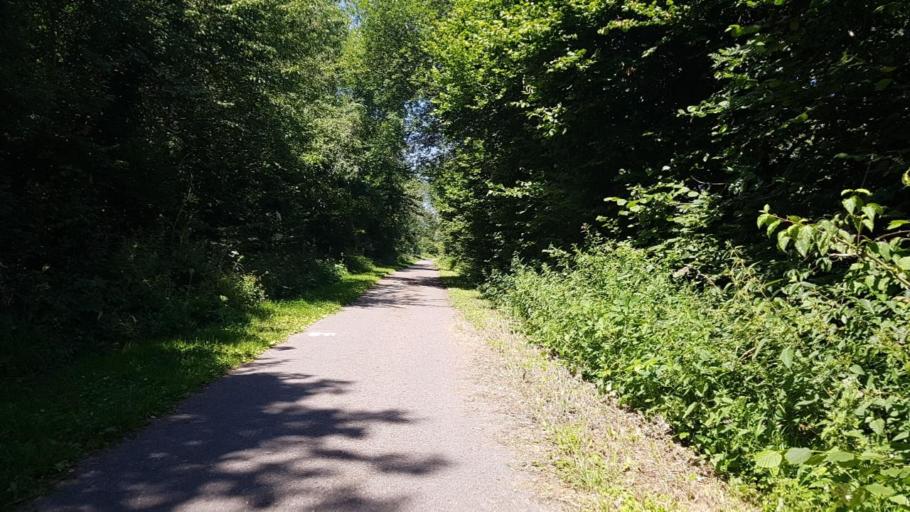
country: BE
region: Wallonia
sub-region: Province du Hainaut
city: Beaumont
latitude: 50.2314
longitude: 4.2435
